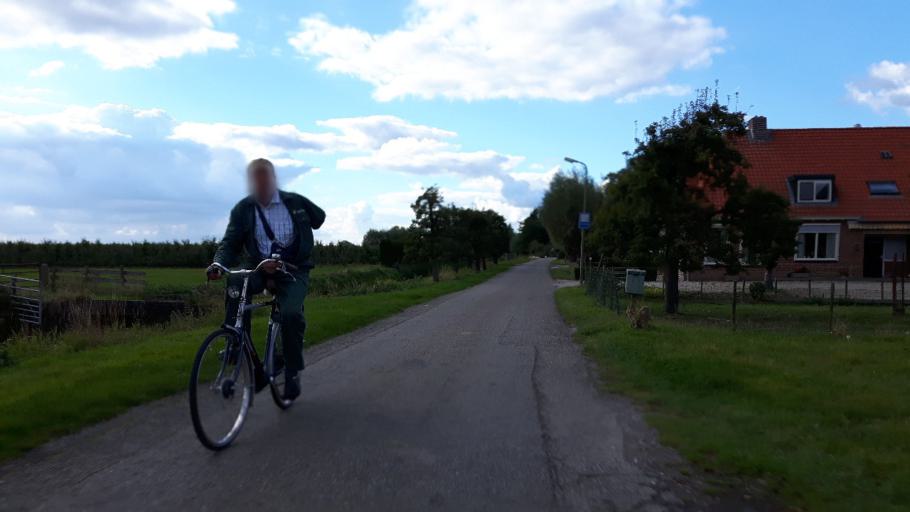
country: NL
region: South Holland
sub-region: Gemeente Leerdam
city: Leerdam
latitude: 51.9231
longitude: 5.1035
